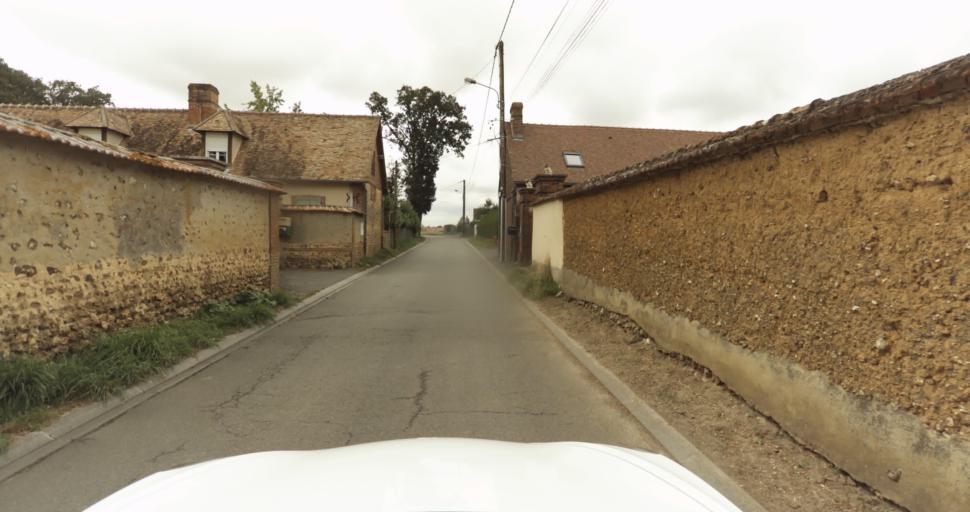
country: FR
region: Haute-Normandie
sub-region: Departement de l'Eure
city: Saint-Sebastien-de-Morsent
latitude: 49.0062
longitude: 1.0666
